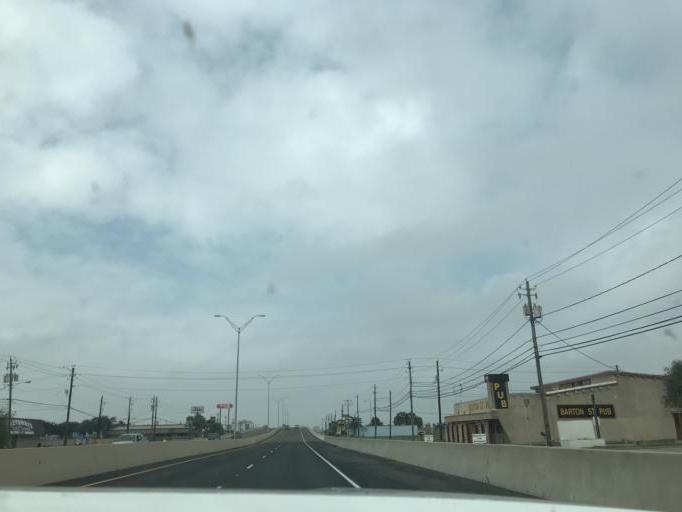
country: US
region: Texas
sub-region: Nueces County
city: Corpus Christi
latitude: 27.6662
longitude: -97.2777
